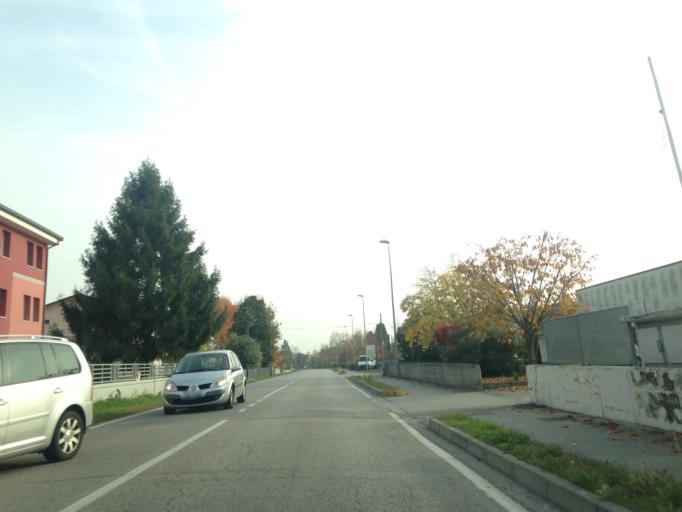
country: IT
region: Friuli Venezia Giulia
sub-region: Provincia di Pordenone
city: Cavolano-Schiavoi
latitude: 45.9217
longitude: 12.5023
